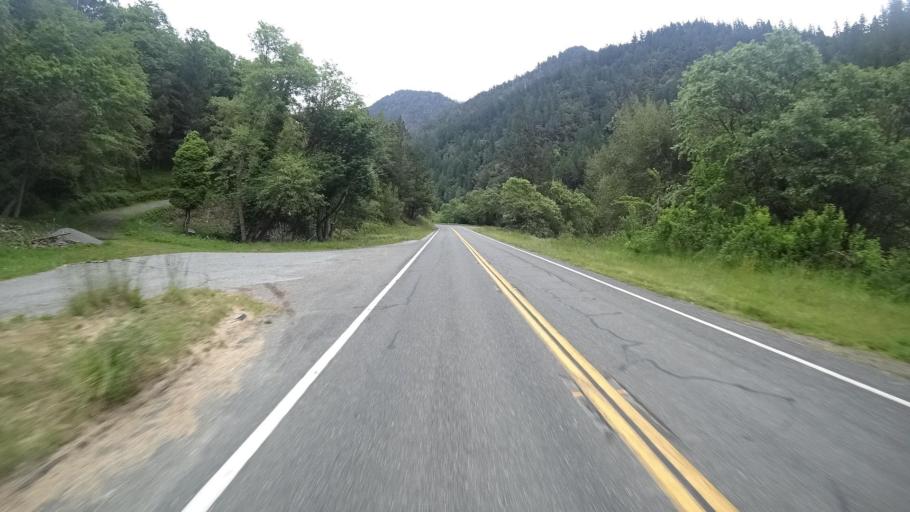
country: US
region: California
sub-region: Humboldt County
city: Willow Creek
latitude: 41.2090
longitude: -123.6592
